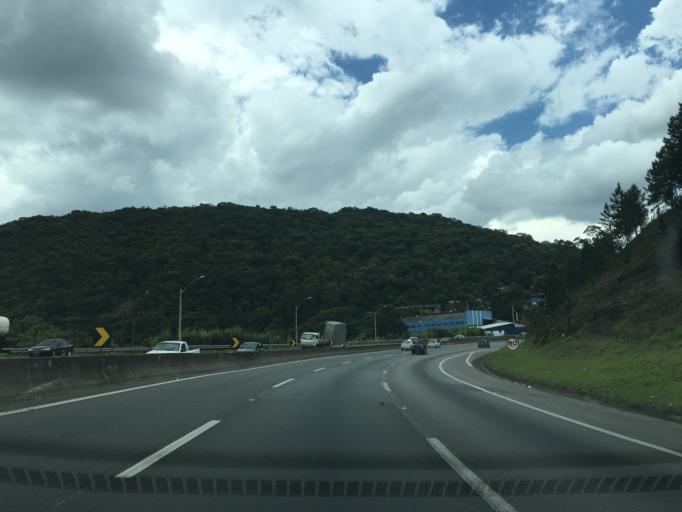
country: BR
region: Sao Paulo
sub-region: Mairipora
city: Mairipora
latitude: -23.2870
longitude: -46.5899
